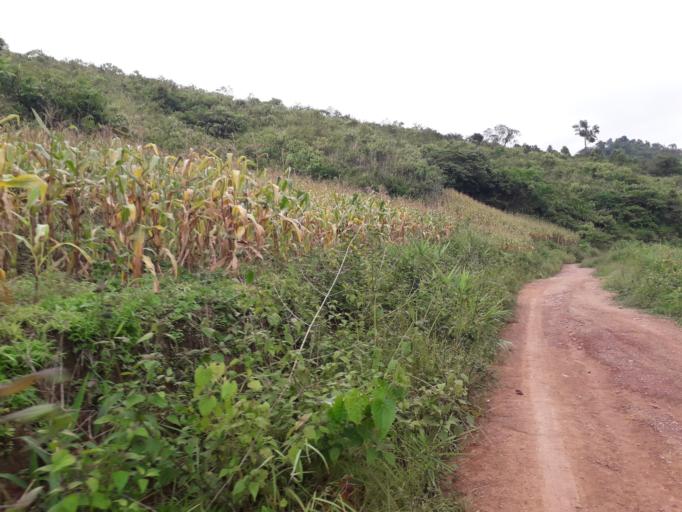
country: CN
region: Yunnan
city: Menglie
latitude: 22.2575
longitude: 101.5975
